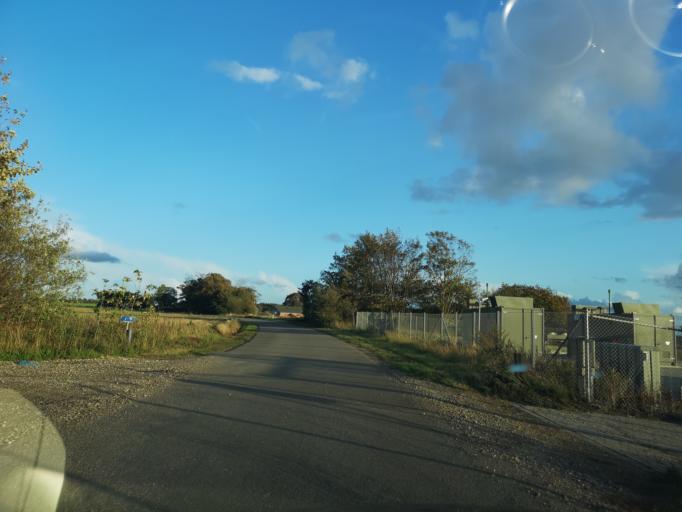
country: DK
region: Central Jutland
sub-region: Ringkobing-Skjern Kommune
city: Skjern
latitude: 55.9866
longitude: 8.5324
